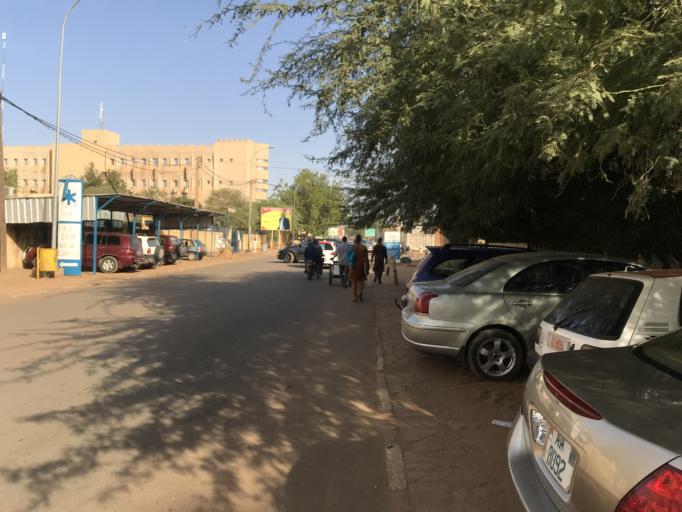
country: NE
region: Niamey
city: Niamey
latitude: 13.5101
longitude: 2.1144
